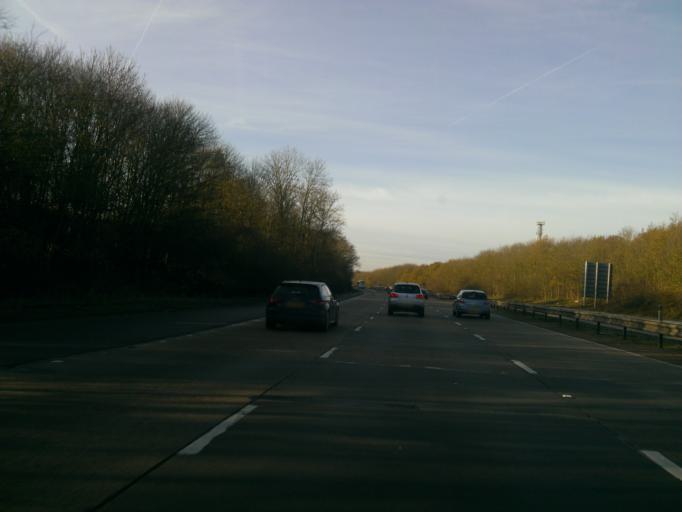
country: GB
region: England
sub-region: Essex
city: Eight Ash Green
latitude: 51.8901
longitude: 0.8224
